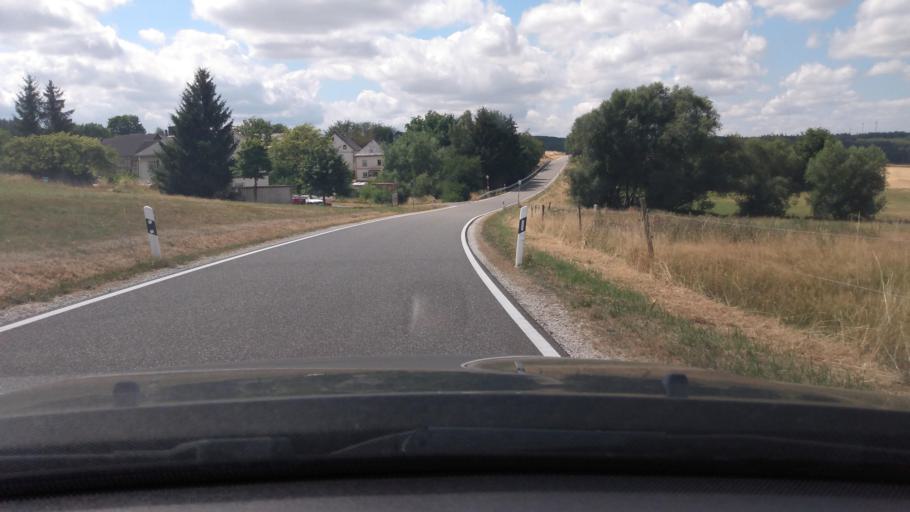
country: DE
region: Rheinland-Pfalz
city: Kleinich
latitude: 49.8769
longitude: 7.1661
